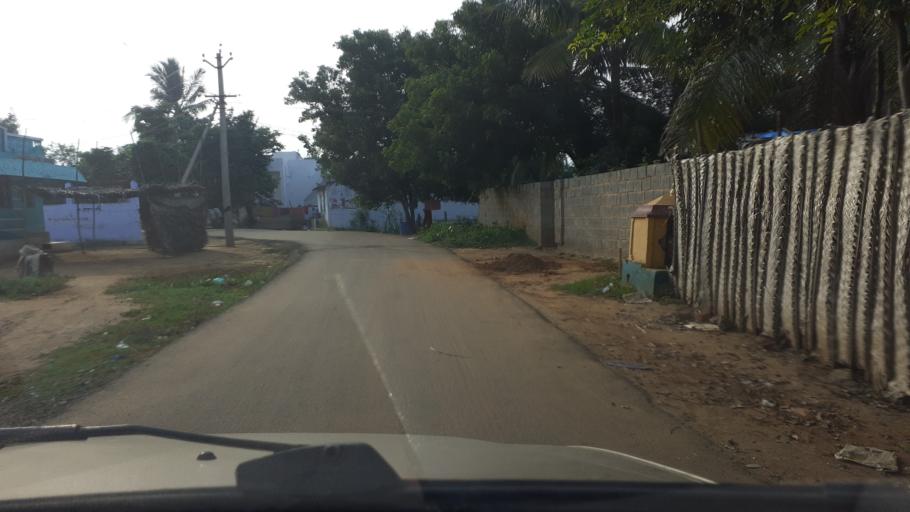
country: IN
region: Tamil Nadu
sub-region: Tirunelveli Kattabo
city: Kalakkadu
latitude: 8.4744
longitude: 77.5900
